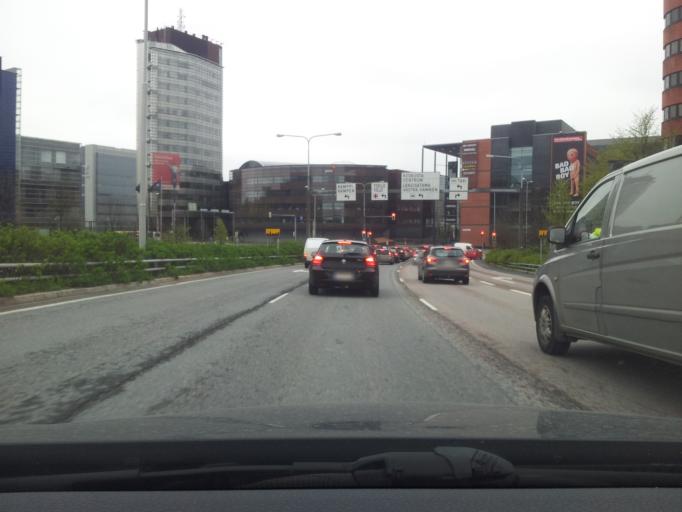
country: FI
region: Uusimaa
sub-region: Helsinki
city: Helsinki
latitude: 60.1653
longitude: 24.9114
